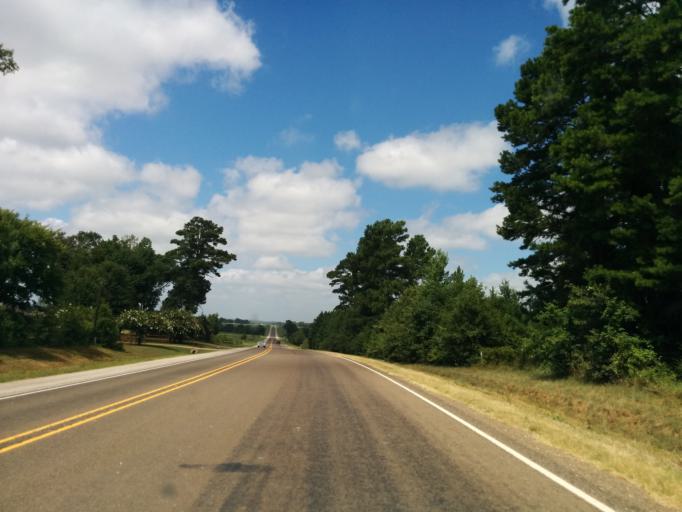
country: US
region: Texas
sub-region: Houston County
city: Hickory Creek
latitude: 31.3247
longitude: -95.3732
